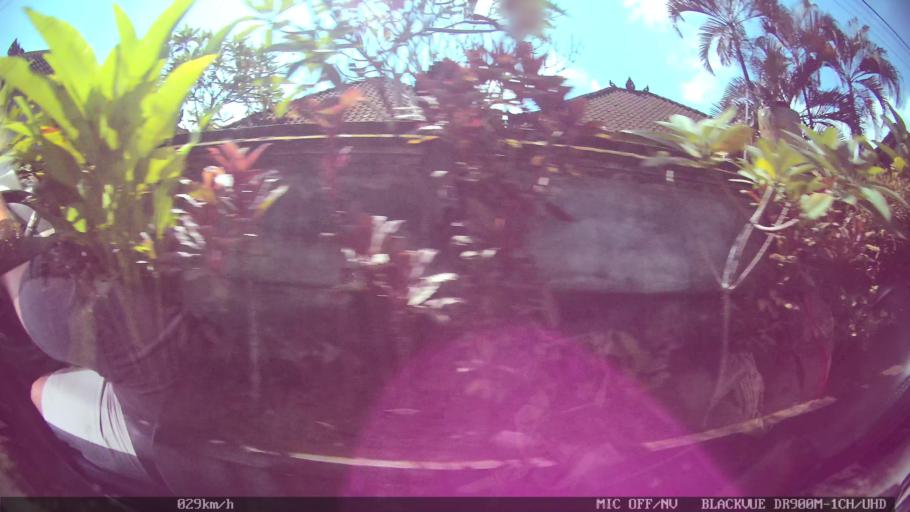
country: ID
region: Bali
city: Banjar Sedang
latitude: -8.5589
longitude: 115.2690
